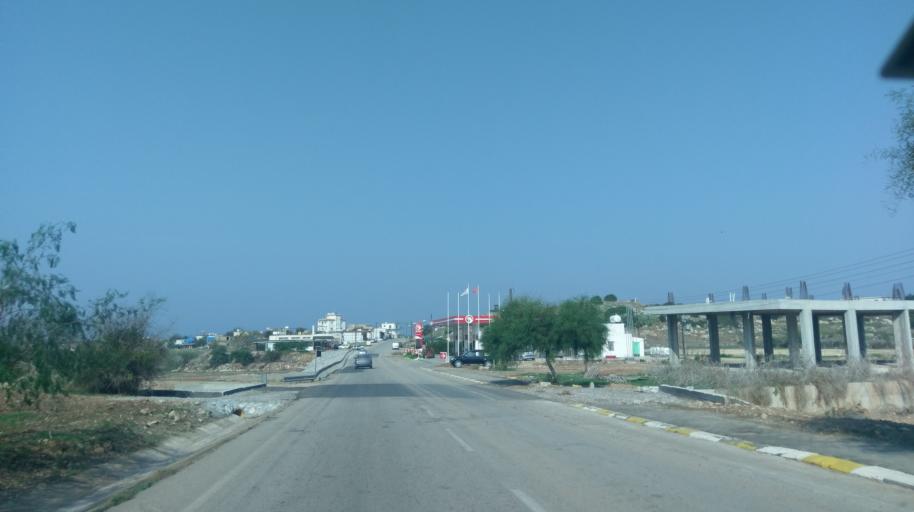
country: CY
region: Ammochostos
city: Leonarisso
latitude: 35.5051
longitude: 34.1613
